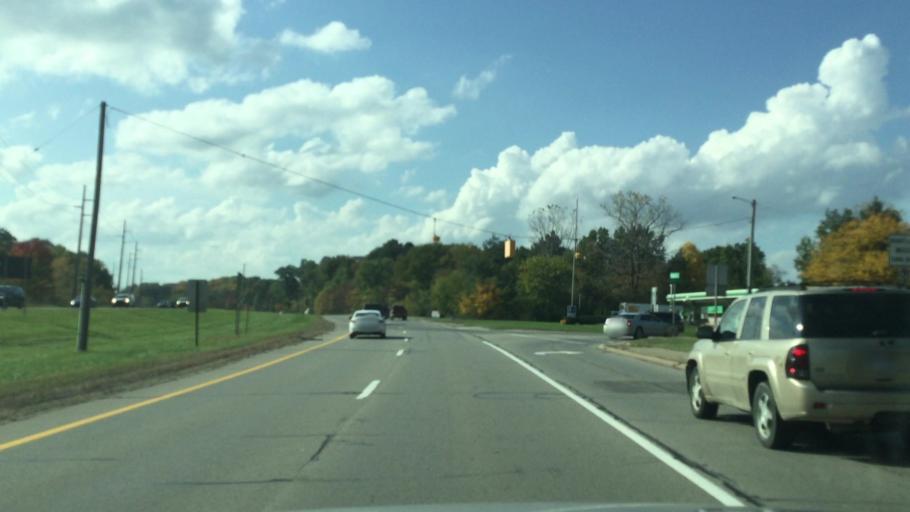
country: US
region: Michigan
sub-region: Oakland County
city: Milford
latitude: 42.6542
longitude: -83.5520
